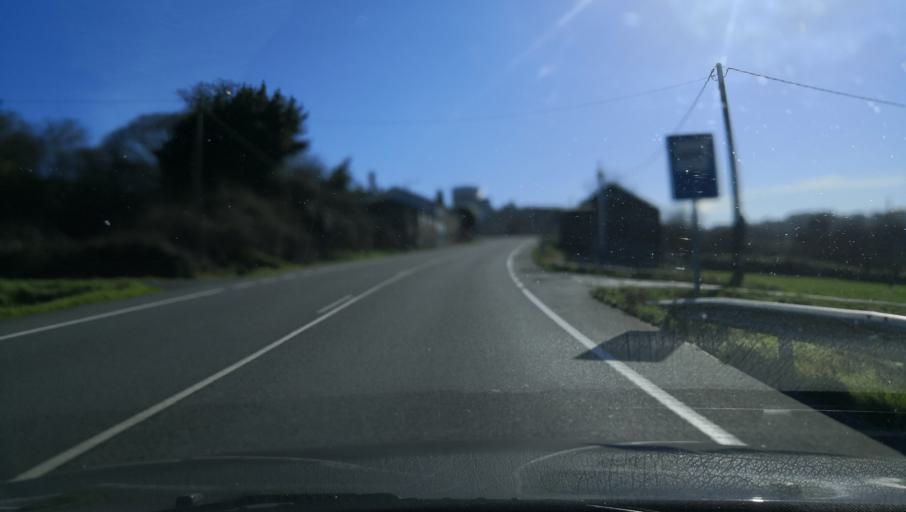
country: ES
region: Galicia
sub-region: Provincia de Pontevedra
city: Silleda
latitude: 42.7076
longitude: -8.2663
